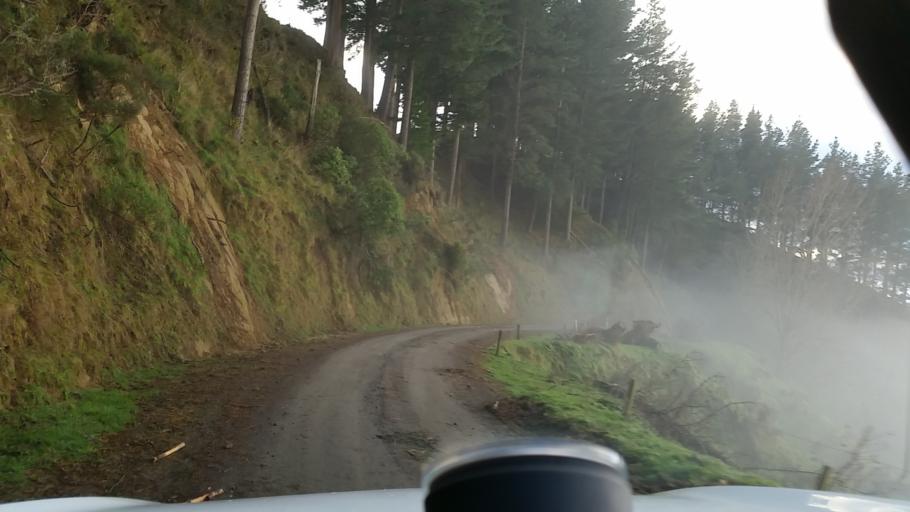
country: NZ
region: Taranaki
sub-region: South Taranaki District
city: Eltham
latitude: -39.4497
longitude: 174.4575
